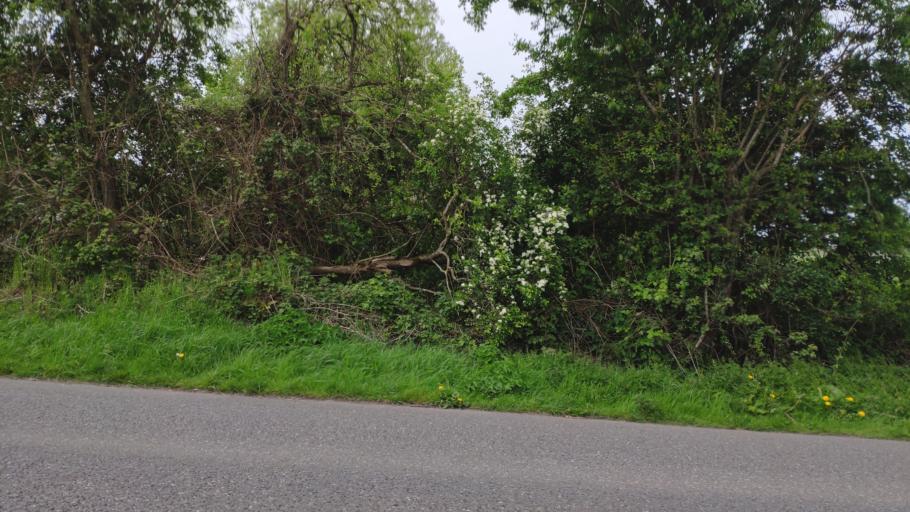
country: IE
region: Munster
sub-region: County Cork
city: Cork
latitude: 51.9225
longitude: -8.4559
